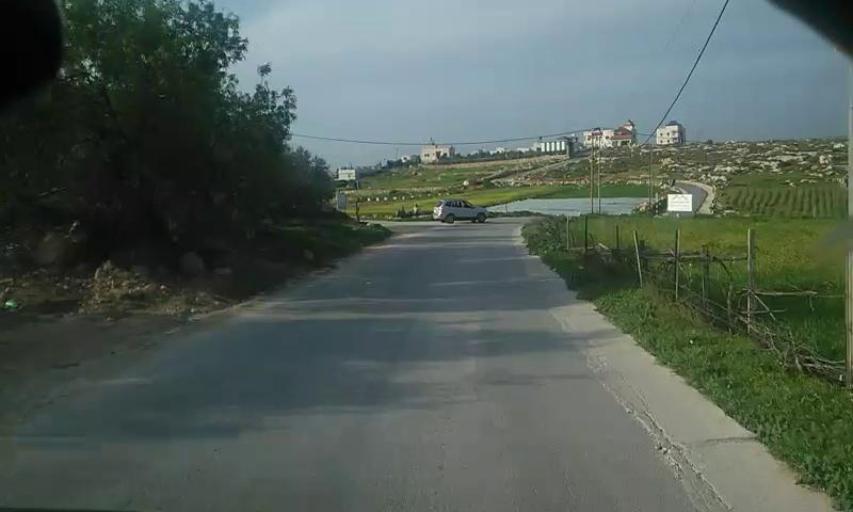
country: PS
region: West Bank
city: Nuba
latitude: 31.6101
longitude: 35.0160
